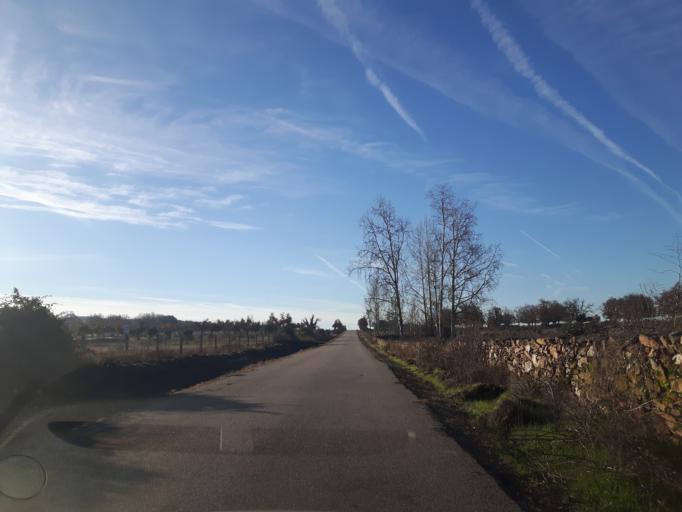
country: ES
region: Castille and Leon
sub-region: Provincia de Salamanca
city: Olmedo de Camaces
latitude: 40.9146
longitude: -6.6176
